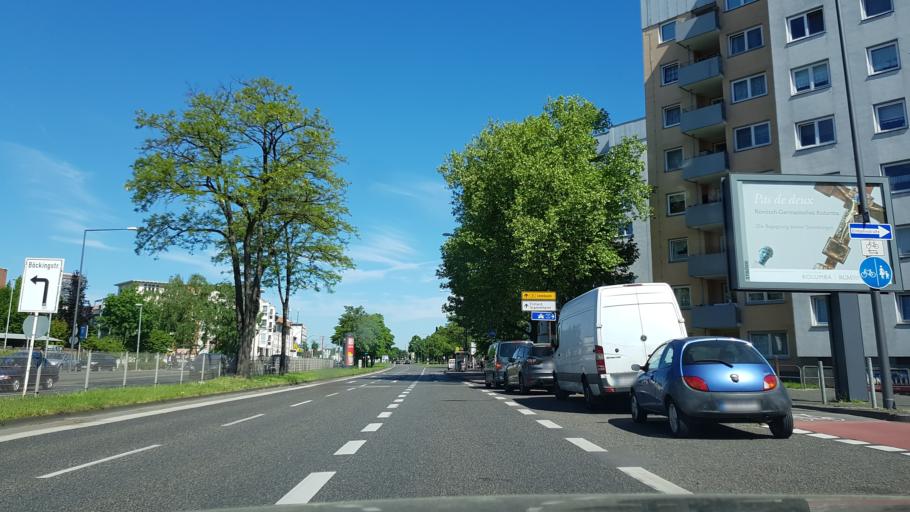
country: DE
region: North Rhine-Westphalia
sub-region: Regierungsbezirk Koln
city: Muelheim
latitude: 50.9726
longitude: 7.0066
